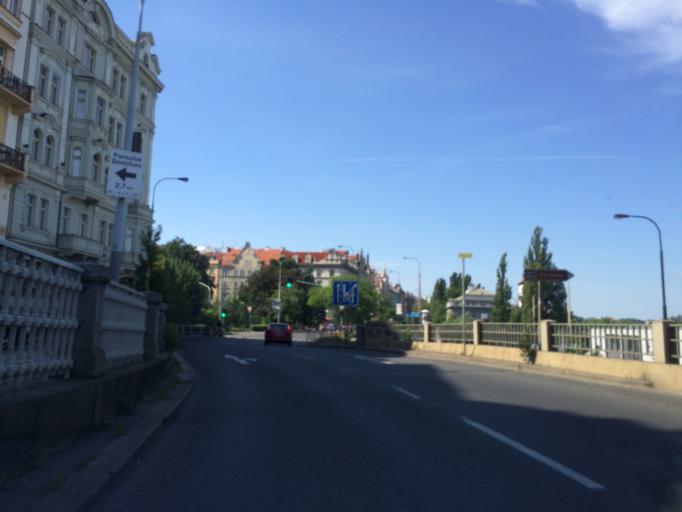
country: CZ
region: Praha
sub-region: Praha 2
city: Vysehrad
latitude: 50.0741
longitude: 14.4096
